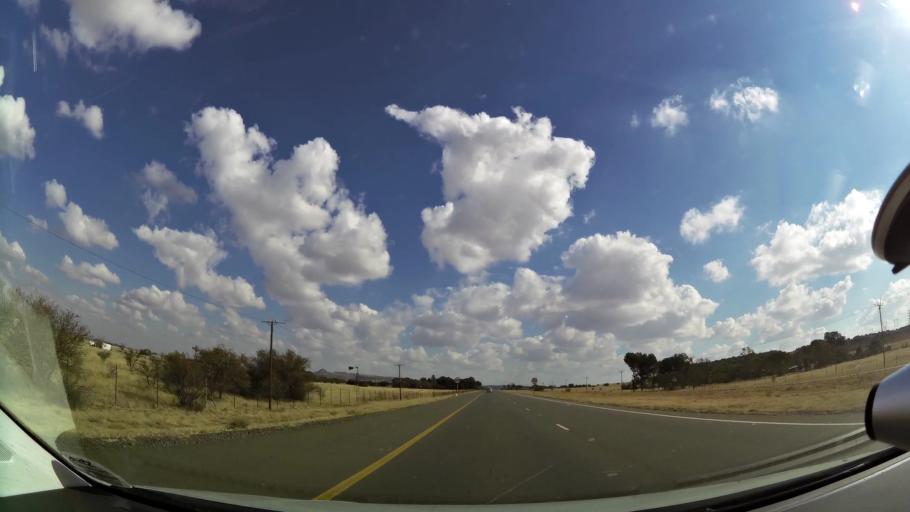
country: ZA
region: Orange Free State
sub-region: Mangaung Metropolitan Municipality
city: Bloemfontein
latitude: -29.1376
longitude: 26.1208
